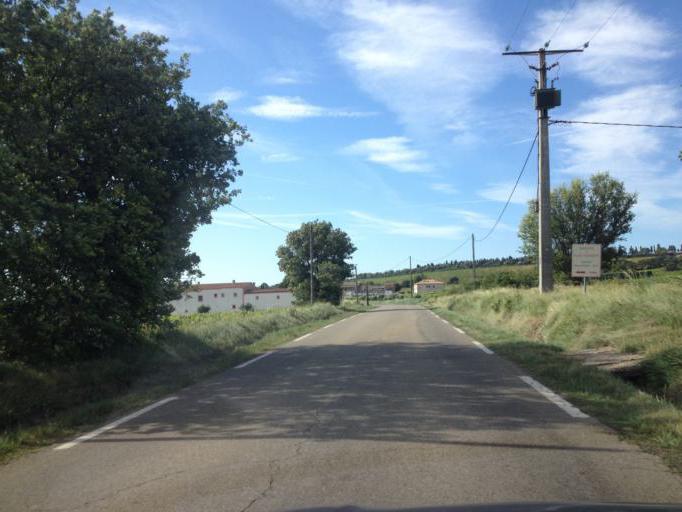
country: FR
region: Provence-Alpes-Cote d'Azur
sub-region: Departement du Vaucluse
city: Chateauneuf-du-Pape
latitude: 44.0932
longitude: 4.8261
